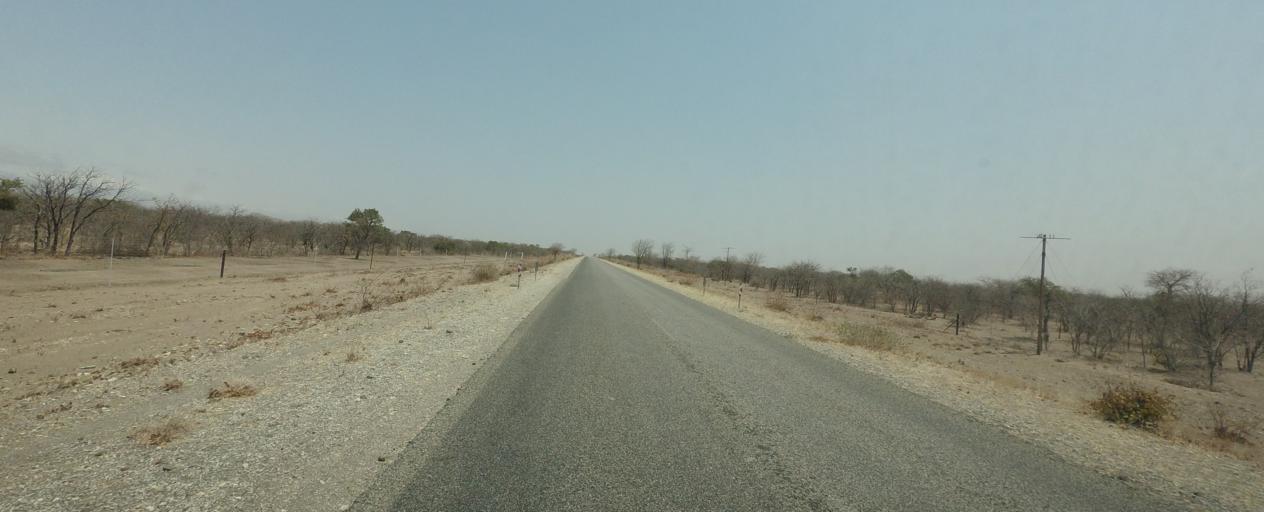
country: ZA
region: Limpopo
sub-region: Vhembe District Municipality
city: Messina
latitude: -22.5254
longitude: 30.4060
